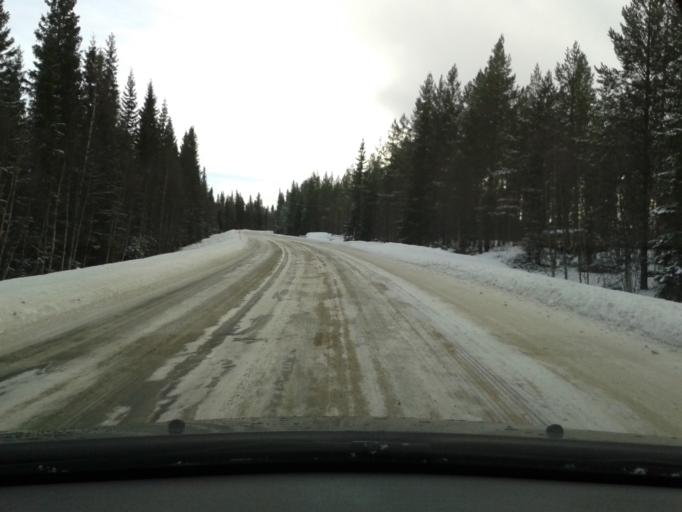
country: SE
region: Vaesterbotten
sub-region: Vilhelmina Kommun
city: Sjoberg
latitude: 64.7575
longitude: 16.1583
